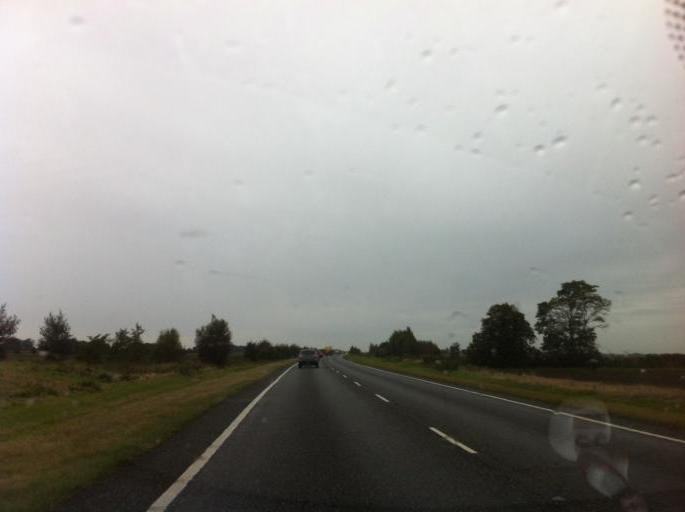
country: GB
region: England
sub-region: Lincolnshire
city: Crowland
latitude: 52.6725
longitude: -0.1546
